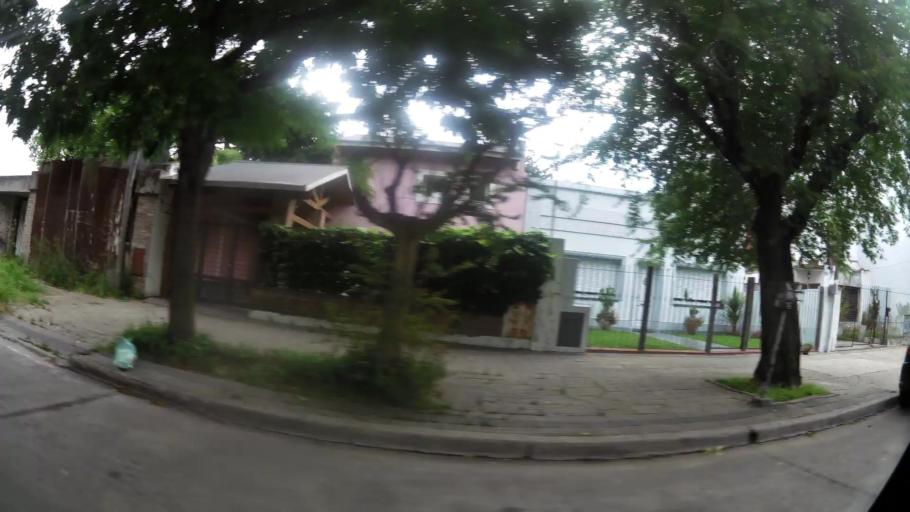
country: AR
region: Buenos Aires
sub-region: Partido de La Plata
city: La Plata
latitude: -34.9290
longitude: -57.9775
